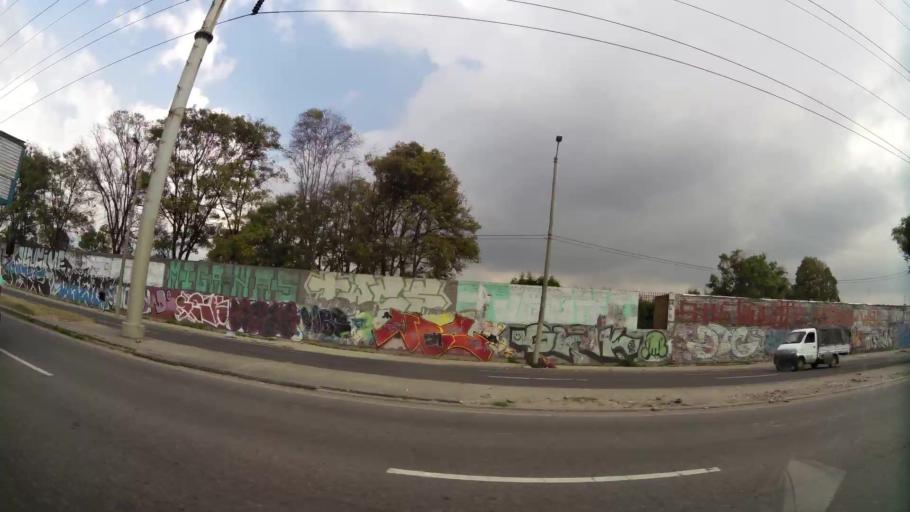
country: CO
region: Bogota D.C.
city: Bogota
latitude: 4.5906
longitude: -74.1184
